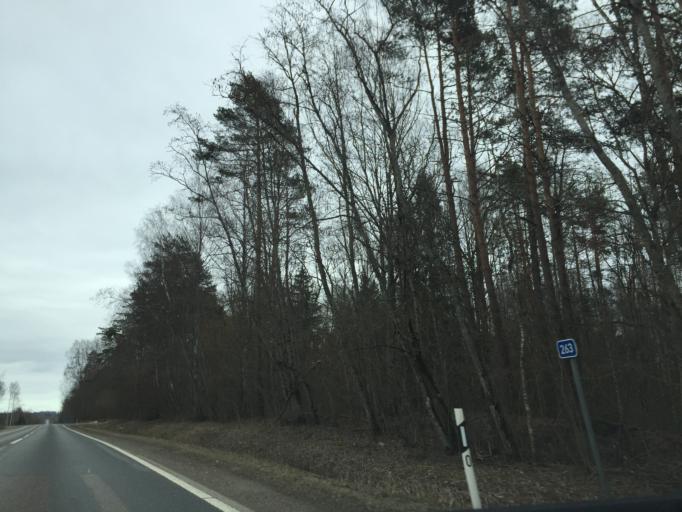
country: LV
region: Kraslavas Rajons
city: Kraslava
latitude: 55.9133
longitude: 27.0438
